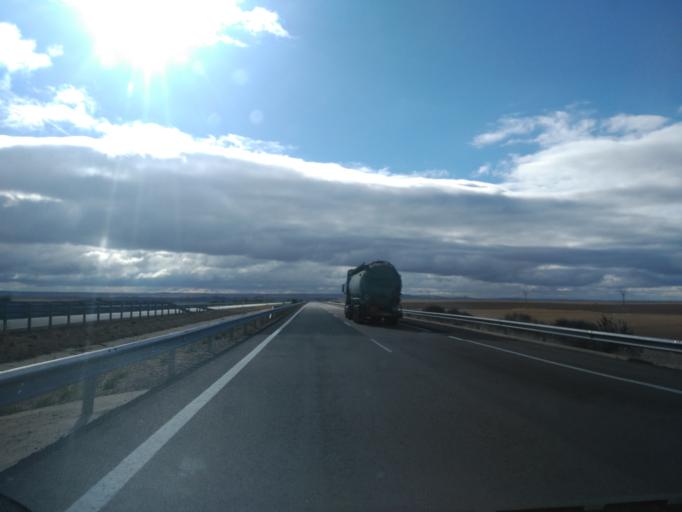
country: ES
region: Castille and Leon
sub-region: Provincia de Palencia
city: Marcilla de Campos
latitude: 42.2966
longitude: -4.3994
